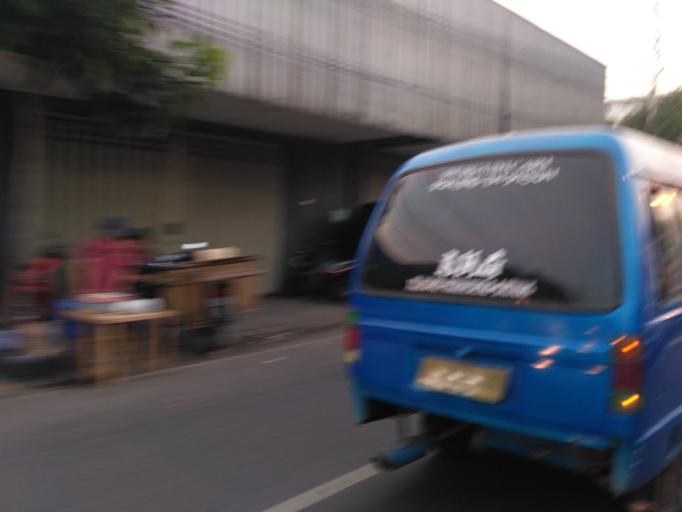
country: ID
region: East Java
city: Gadang
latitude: -7.9974
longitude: 112.6326
